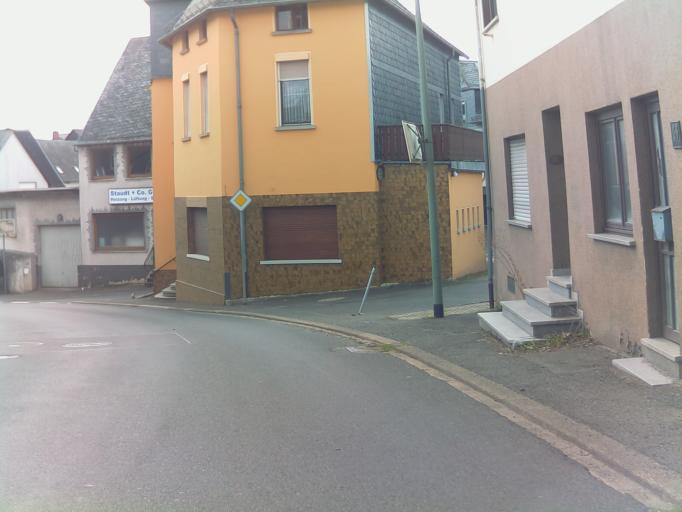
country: DE
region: Rheinland-Pfalz
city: Bruschied
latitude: 49.8426
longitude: 7.3772
